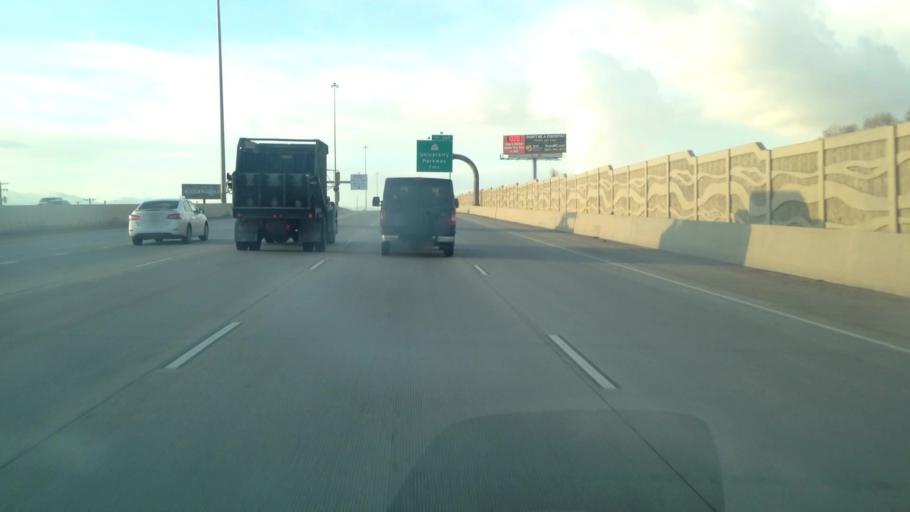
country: US
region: Utah
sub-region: Utah County
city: Orem
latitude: 40.2588
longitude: -111.7031
